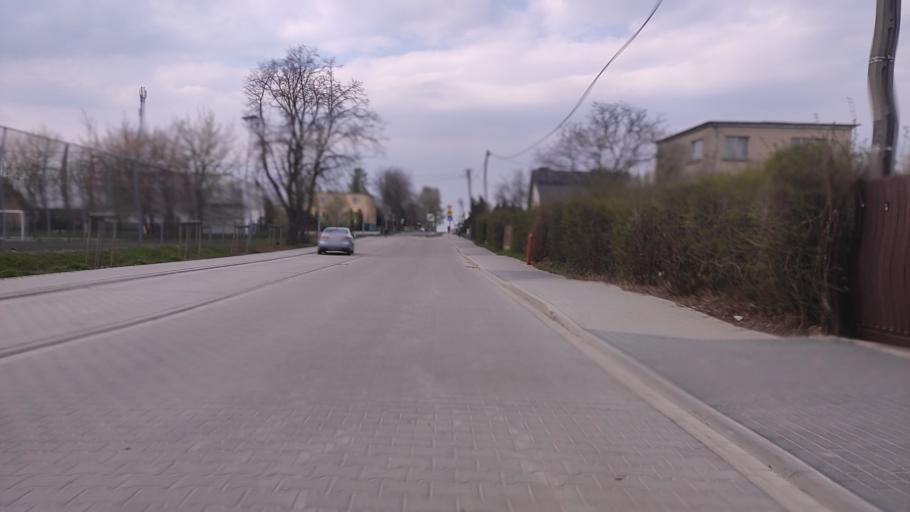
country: PL
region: Greater Poland Voivodeship
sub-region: Powiat poznanski
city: Kostrzyn
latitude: 52.4010
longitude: 17.1630
